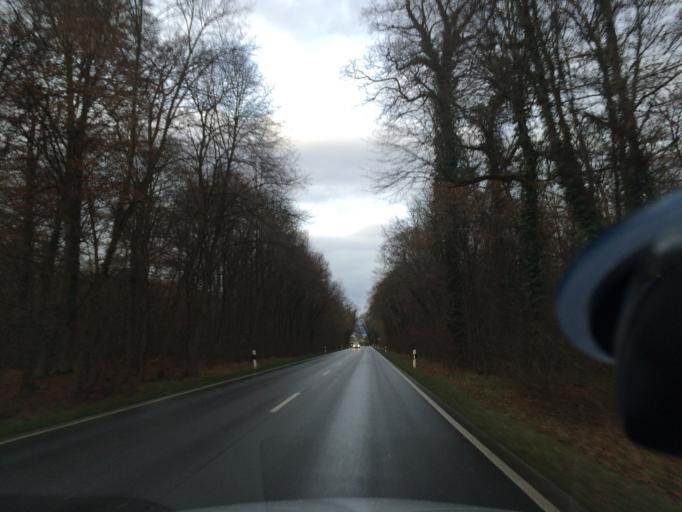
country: DE
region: Hesse
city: Morfelden-Walldorf
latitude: 49.9634
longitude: 8.5746
